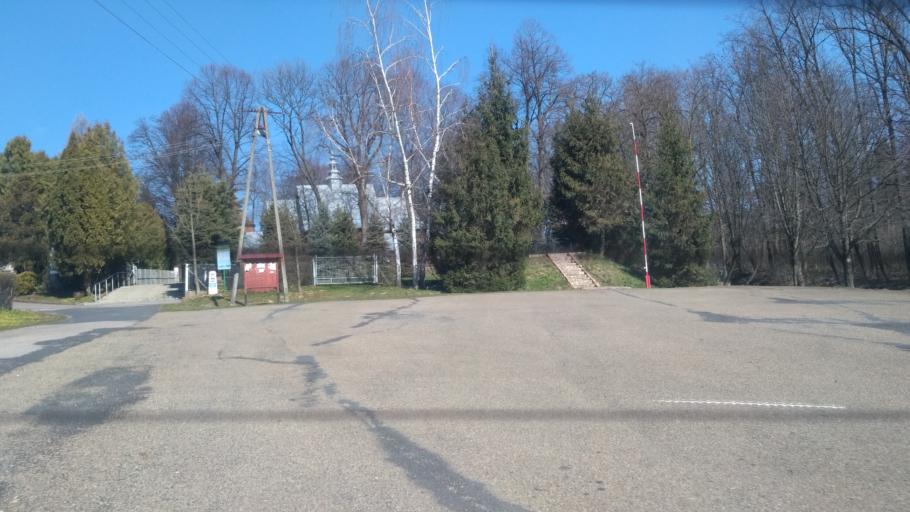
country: PL
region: Subcarpathian Voivodeship
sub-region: Powiat jaroslawski
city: Pawlosiow
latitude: 49.9604
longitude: 22.6714
